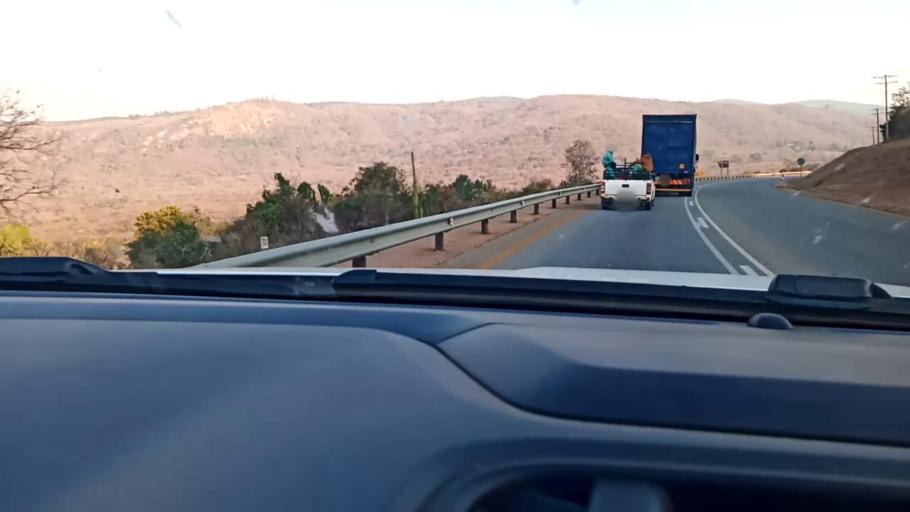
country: ZA
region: Limpopo
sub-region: Mopani District Municipality
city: Ga-Kgapane
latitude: -23.6500
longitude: 30.1720
